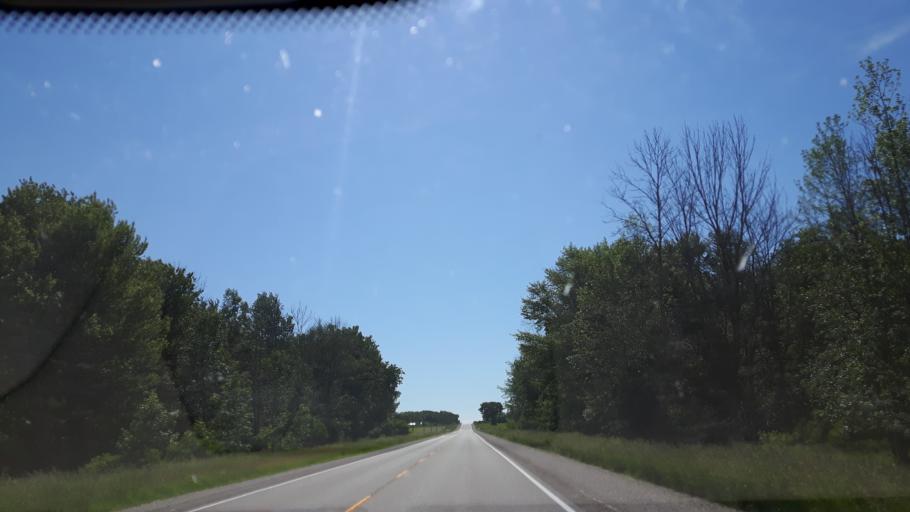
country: CA
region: Ontario
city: Bluewater
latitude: 43.4289
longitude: -81.5513
